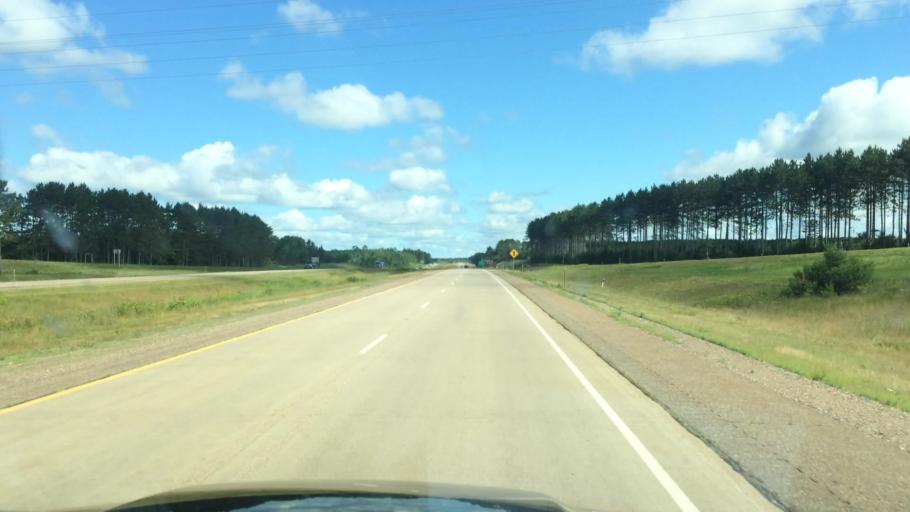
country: US
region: Wisconsin
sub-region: Lincoln County
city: Tomahawk
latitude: 45.4707
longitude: -89.6913
